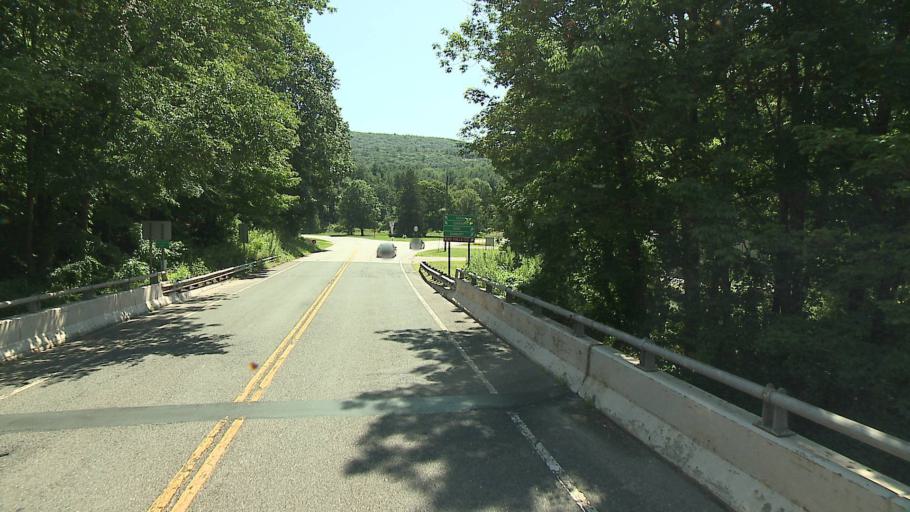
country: US
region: Connecticut
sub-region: Litchfield County
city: Kent
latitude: 41.8192
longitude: -73.3717
